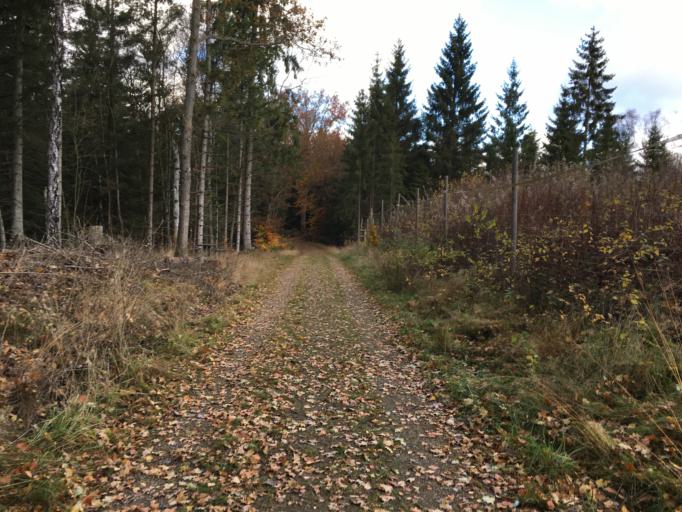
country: SE
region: Skane
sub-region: Hoors Kommun
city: Hoeoer
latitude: 55.9862
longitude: 13.5445
